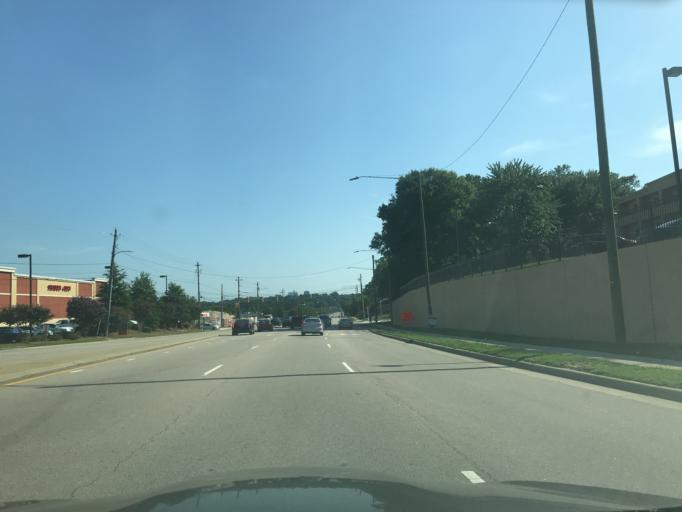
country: US
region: North Carolina
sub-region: Wake County
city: Raleigh
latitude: 35.8244
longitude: -78.6219
